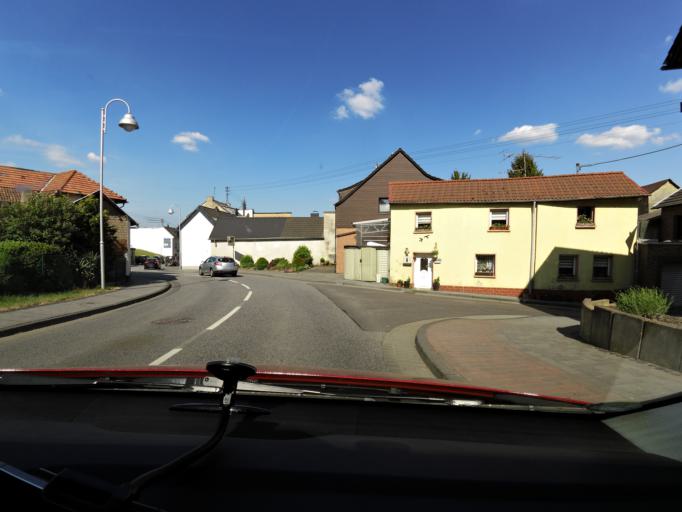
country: DE
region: Rheinland-Pfalz
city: Bad Neuenahr-Ahrweiler
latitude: 50.5707
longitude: 7.0940
